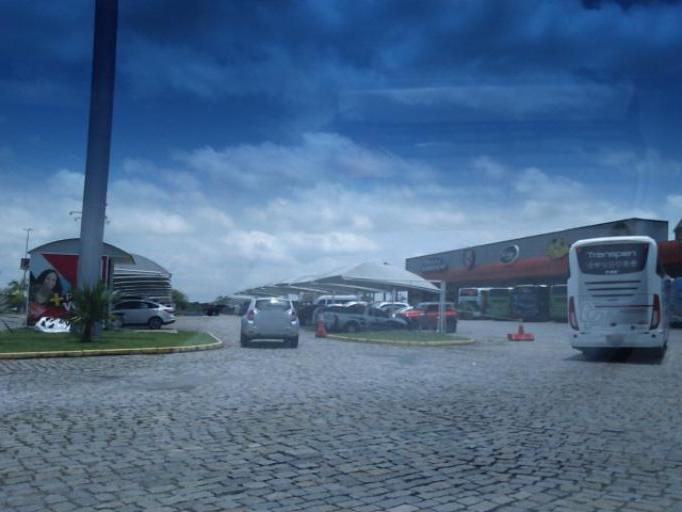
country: BR
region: Sao Paulo
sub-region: Registro
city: Registro
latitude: -24.5295
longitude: -47.8570
